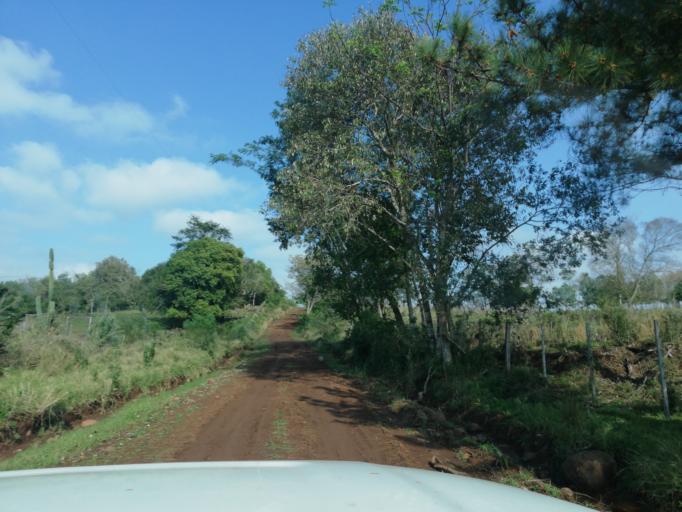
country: AR
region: Misiones
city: Cerro Azul
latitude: -27.5985
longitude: -55.5264
